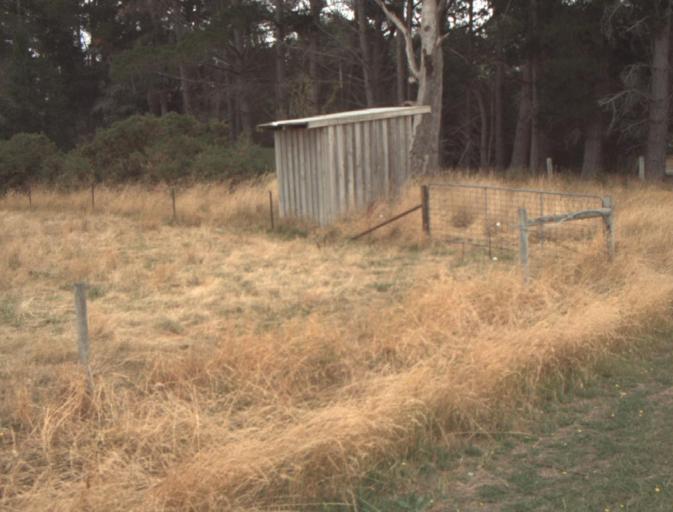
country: AU
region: Tasmania
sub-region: Northern Midlands
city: Evandale
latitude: -41.5053
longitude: 147.4818
